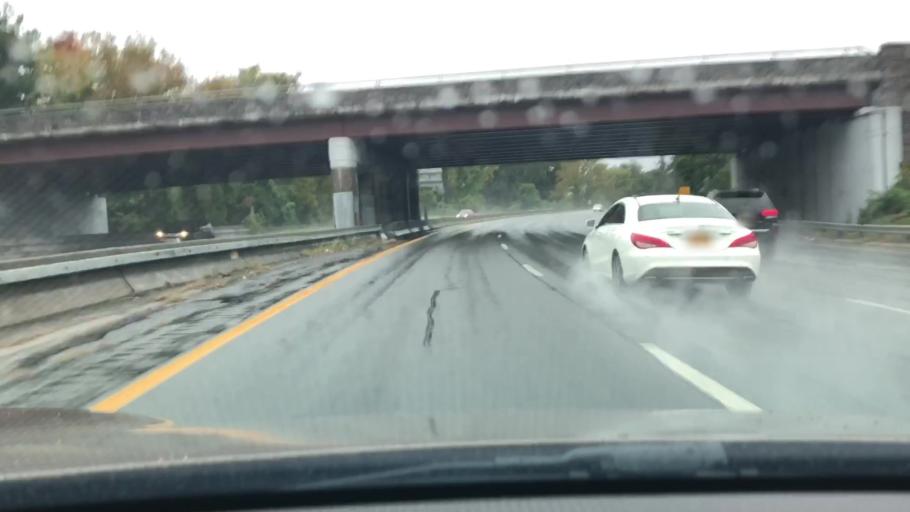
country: US
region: New York
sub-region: Westchester County
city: Bronxville
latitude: 40.9519
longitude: -73.8532
